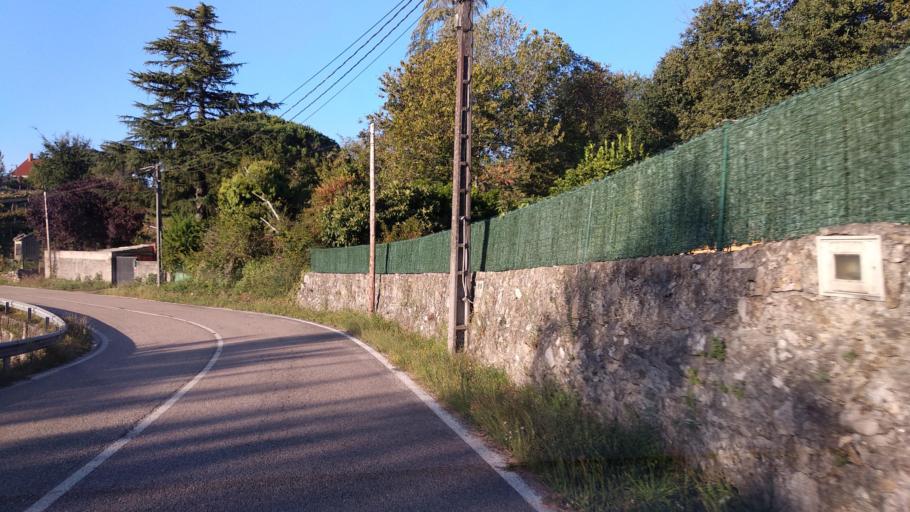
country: ES
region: Galicia
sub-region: Provincia de Pontevedra
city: Ponte Caldelas
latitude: 42.3615
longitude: -8.5309
